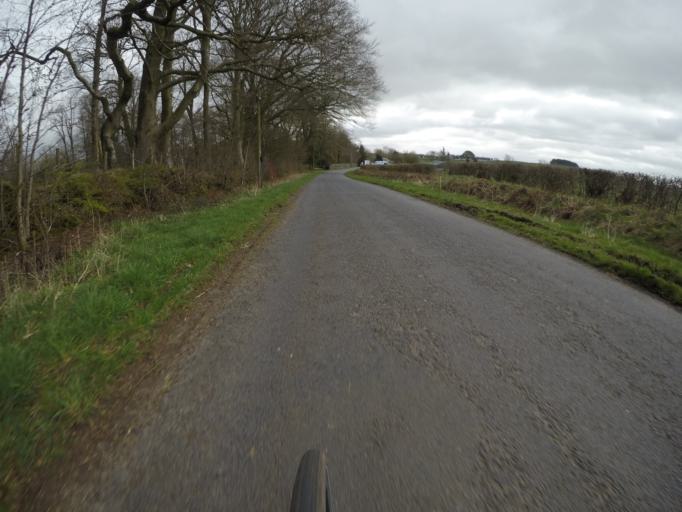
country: GB
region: Scotland
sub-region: East Ayrshire
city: Kilmaurs
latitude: 55.6702
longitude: -4.5727
